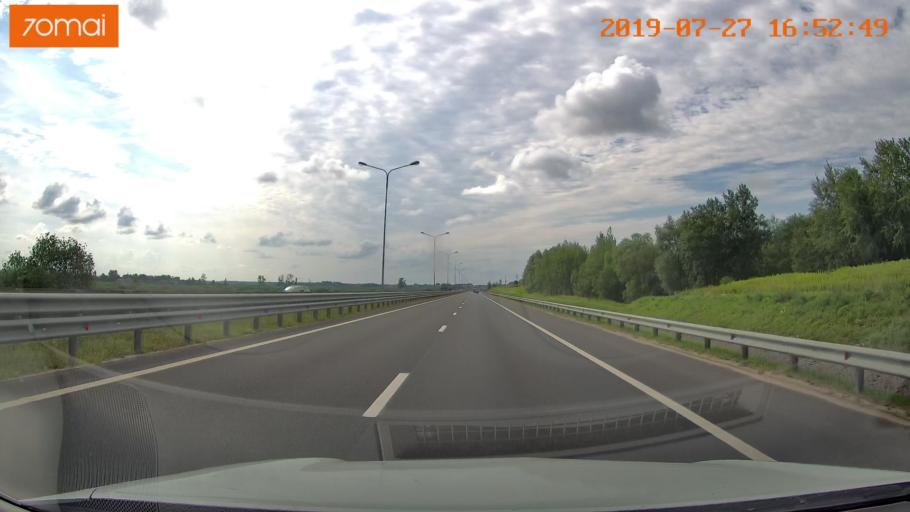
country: RU
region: Kaliningrad
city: Gvardeysk
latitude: 54.6849
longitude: 20.8468
